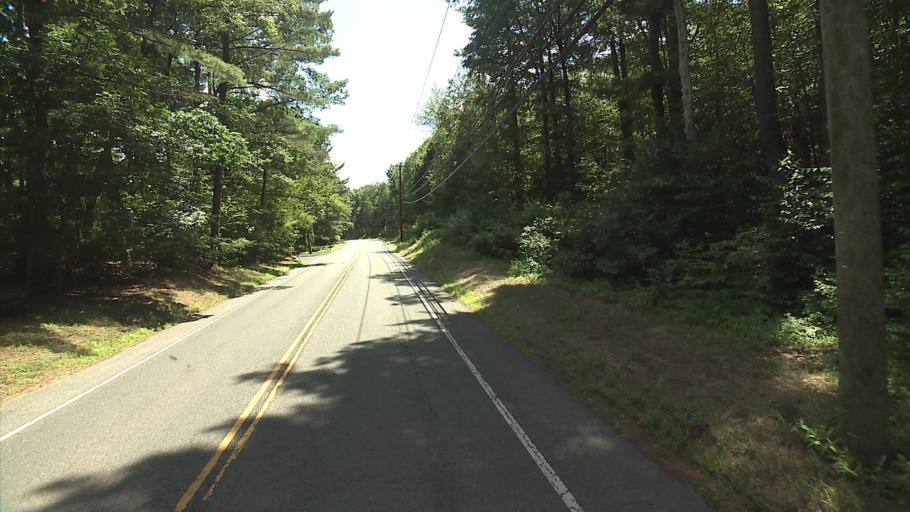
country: US
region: Massachusetts
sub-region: Hampden County
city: Southwick
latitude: 42.0020
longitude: -72.7254
